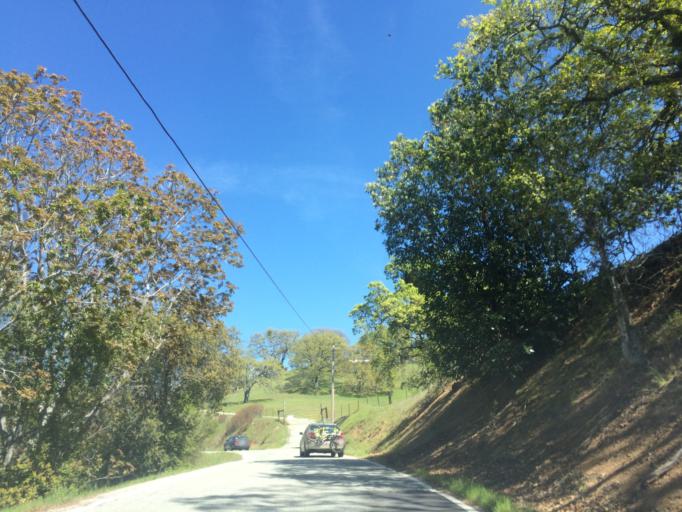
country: US
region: California
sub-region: Santa Clara County
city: Morgan Hill
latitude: 37.1845
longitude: -121.5570
